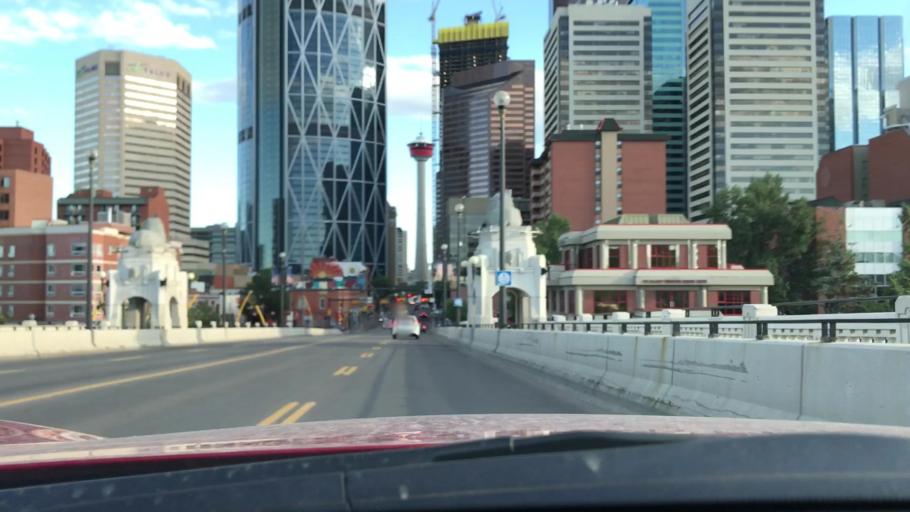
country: CA
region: Alberta
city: Calgary
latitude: 51.0527
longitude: -114.0626
